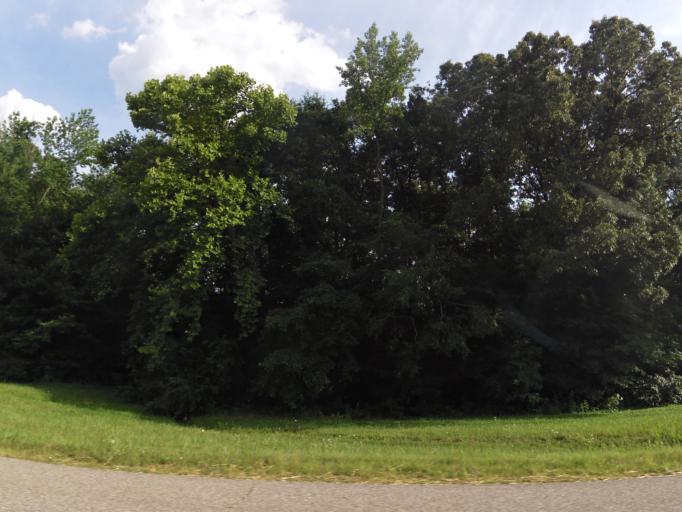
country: US
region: Tennessee
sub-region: Benton County
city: Camden
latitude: 36.0265
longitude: -88.0849
